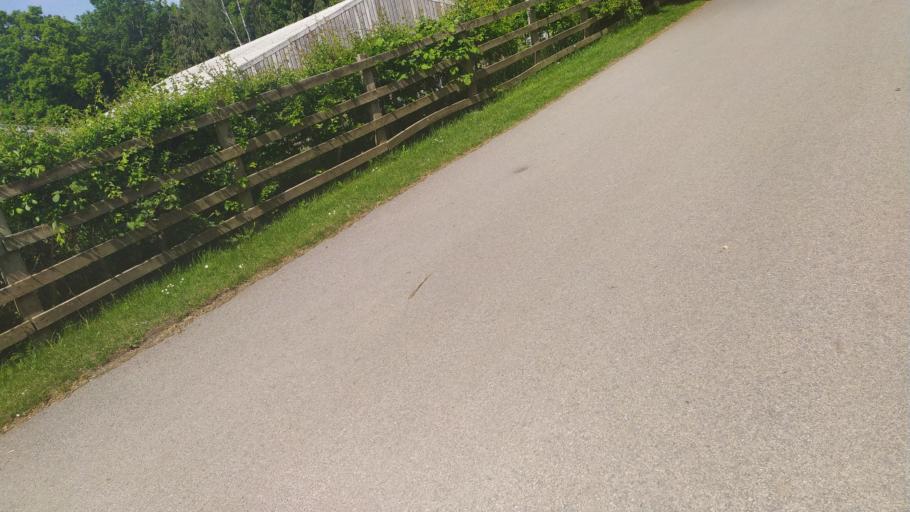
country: GB
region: England
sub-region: North Yorkshire
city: Pannal
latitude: 53.8977
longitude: -1.5355
